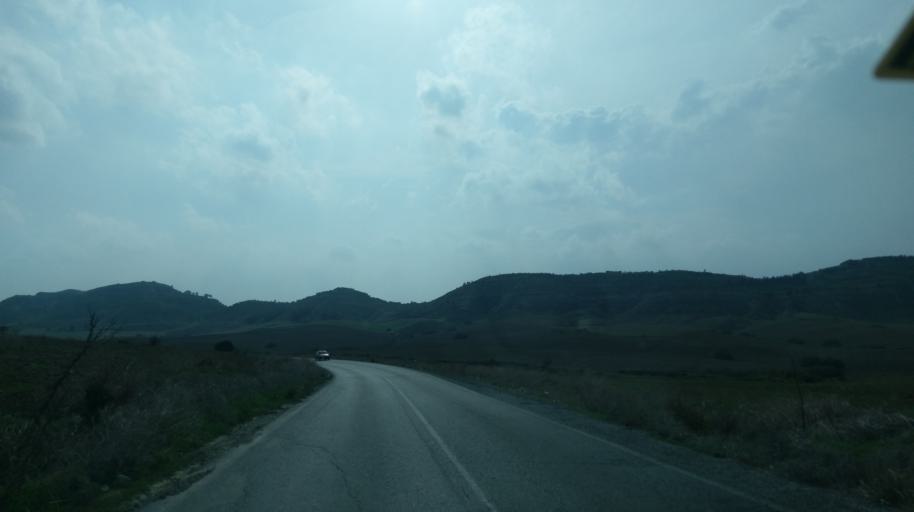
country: CY
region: Keryneia
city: Lapithos
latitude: 35.2610
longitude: 33.1306
